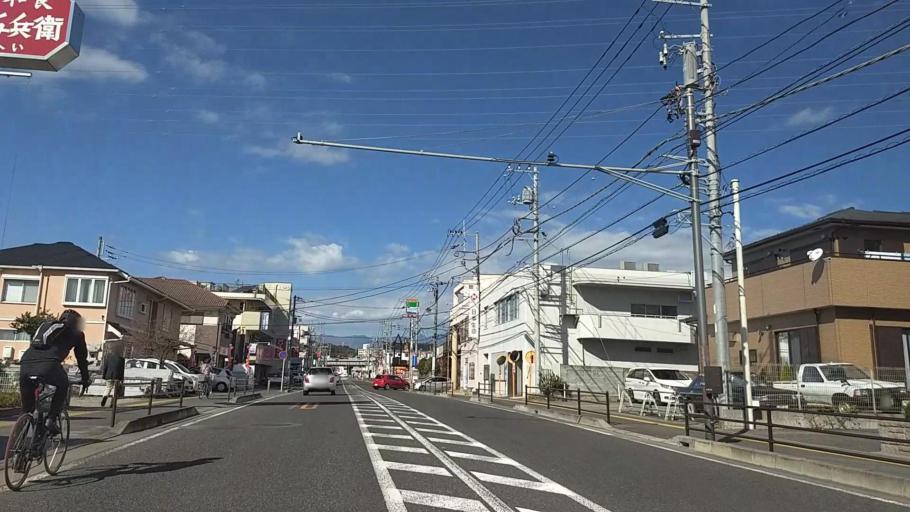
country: JP
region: Kanagawa
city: Ninomiya
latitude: 35.3061
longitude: 139.2544
